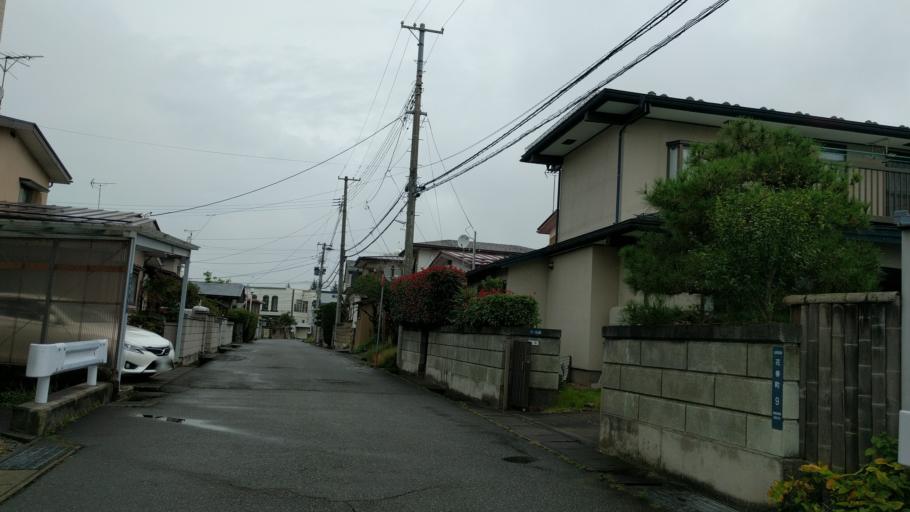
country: JP
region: Fukushima
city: Kitakata
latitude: 37.4901
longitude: 139.9449
